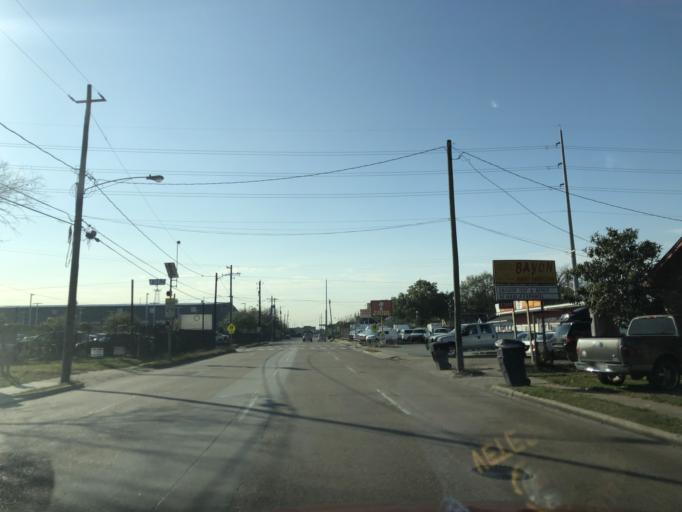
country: US
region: Texas
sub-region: Harris County
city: Houston
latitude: 29.7950
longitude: -95.4117
